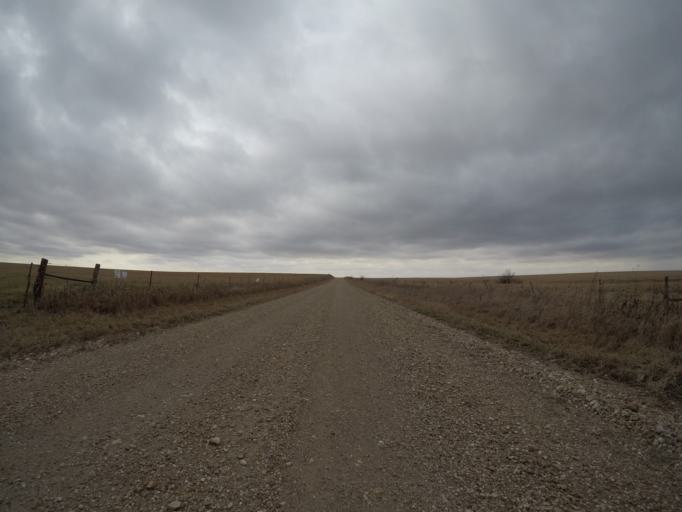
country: US
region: Kansas
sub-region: Wabaunsee County
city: Alma
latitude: 38.7245
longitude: -96.1773
